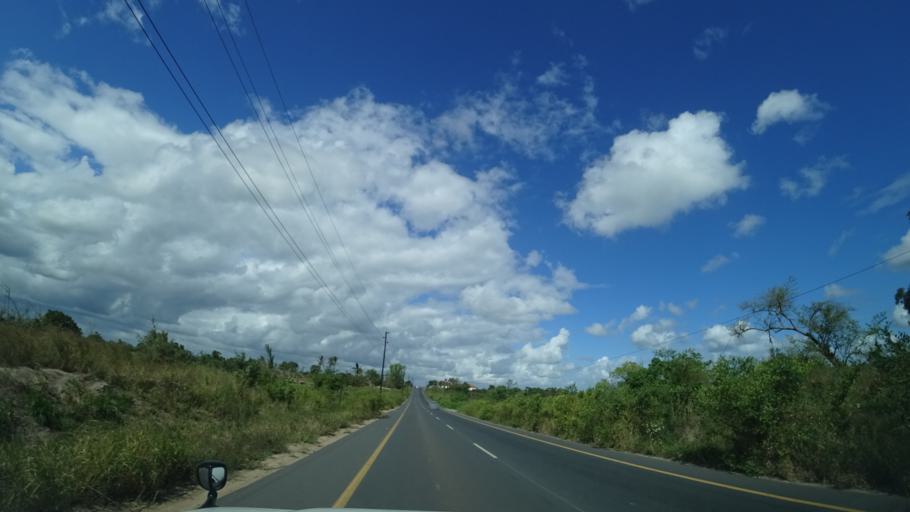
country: MZ
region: Sofala
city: Dondo
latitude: -19.5056
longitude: 34.6050
